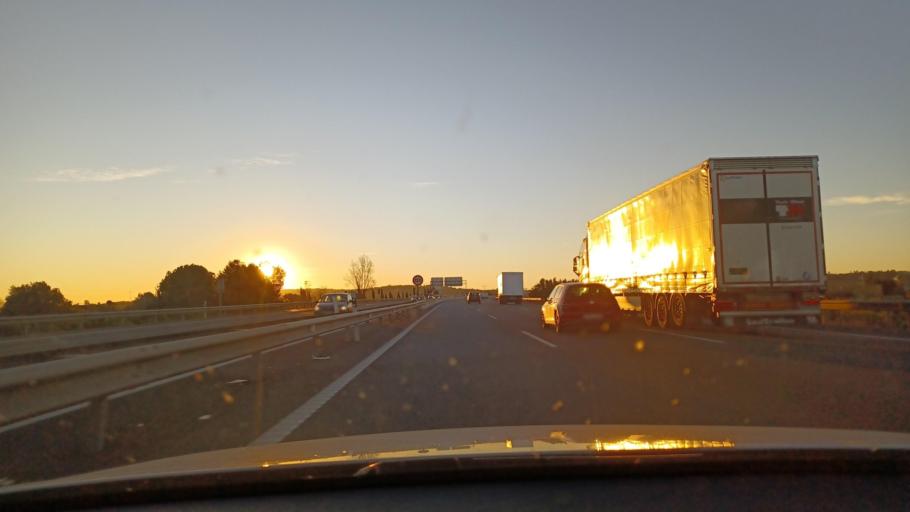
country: ES
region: Valencia
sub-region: Provincia de Valencia
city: Torrent
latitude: 39.4335
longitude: -0.5333
